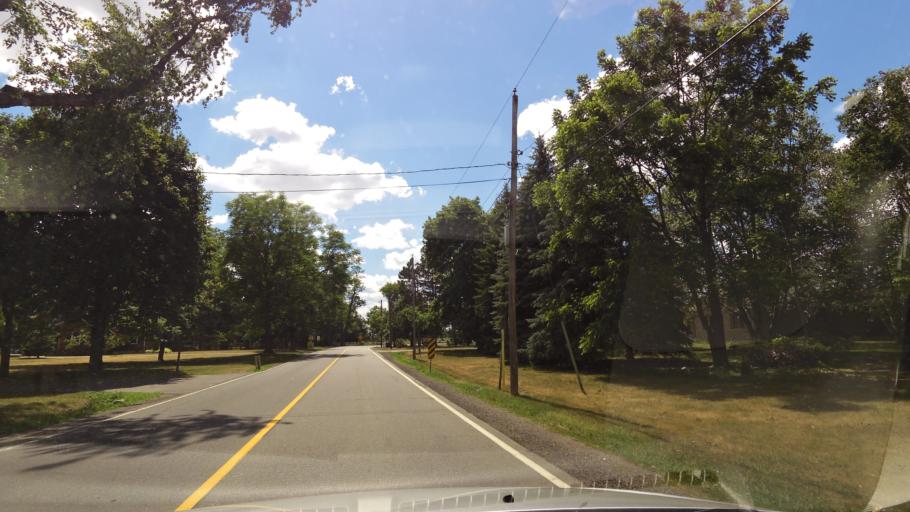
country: CA
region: Ontario
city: Brampton
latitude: 43.6419
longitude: -79.8542
